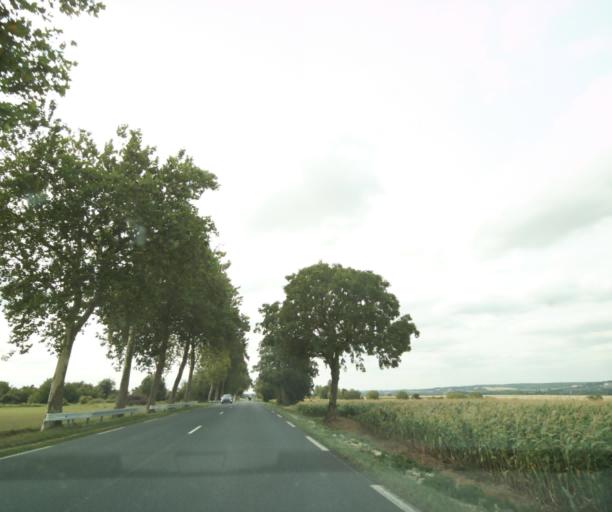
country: FR
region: Centre
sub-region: Departement de l'Indre
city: Buzancais
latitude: 46.9129
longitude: 1.3284
